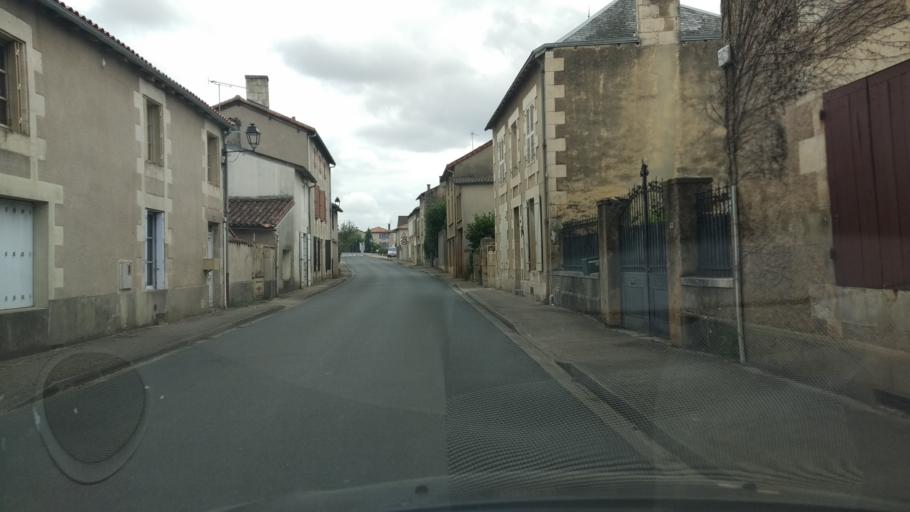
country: FR
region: Poitou-Charentes
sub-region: Departement de la Vienne
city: La Villedieu-du-Clain
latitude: 46.4542
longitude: 0.3670
